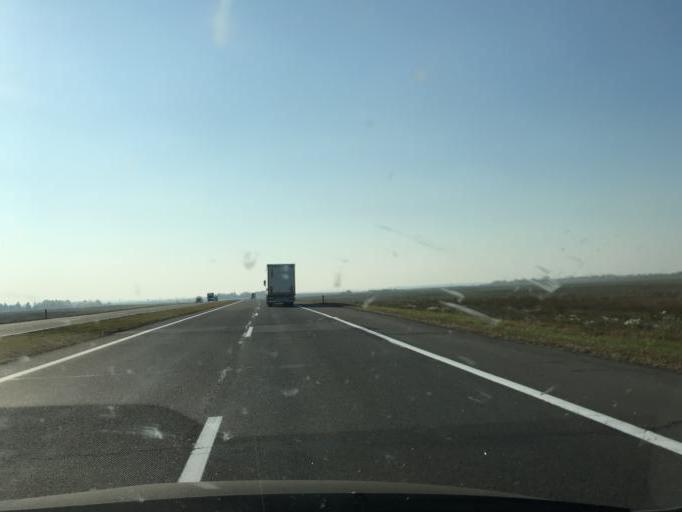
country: BY
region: Minsk
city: Snow
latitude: 53.2907
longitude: 26.3425
